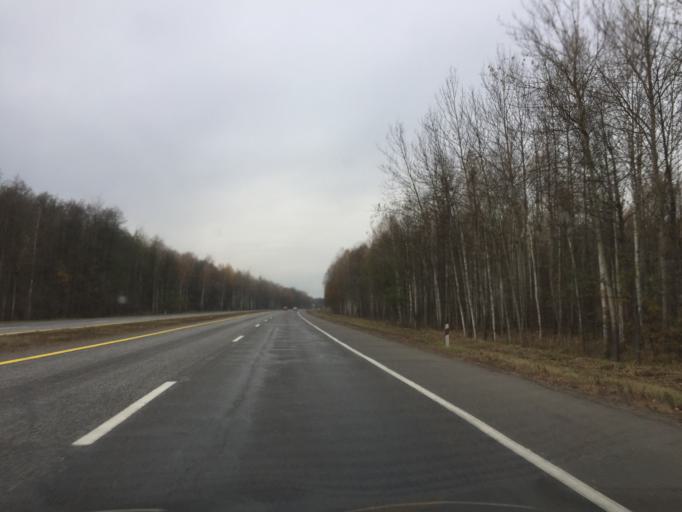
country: BY
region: Gomel
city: Kastsyukowka
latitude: 52.3570
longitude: 30.6985
